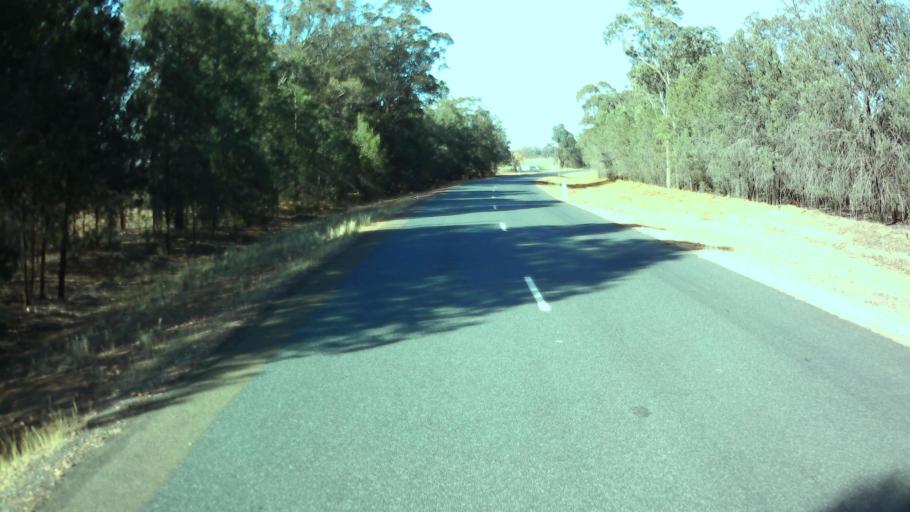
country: AU
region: New South Wales
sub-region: Weddin
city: Grenfell
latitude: -34.0328
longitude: 148.0907
